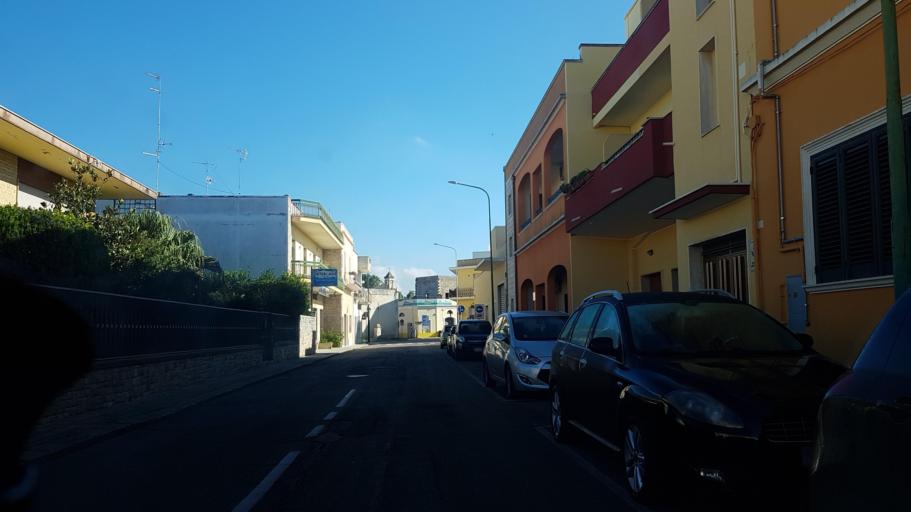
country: IT
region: Apulia
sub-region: Provincia di Lecce
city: Arnesano
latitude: 40.3376
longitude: 18.0878
